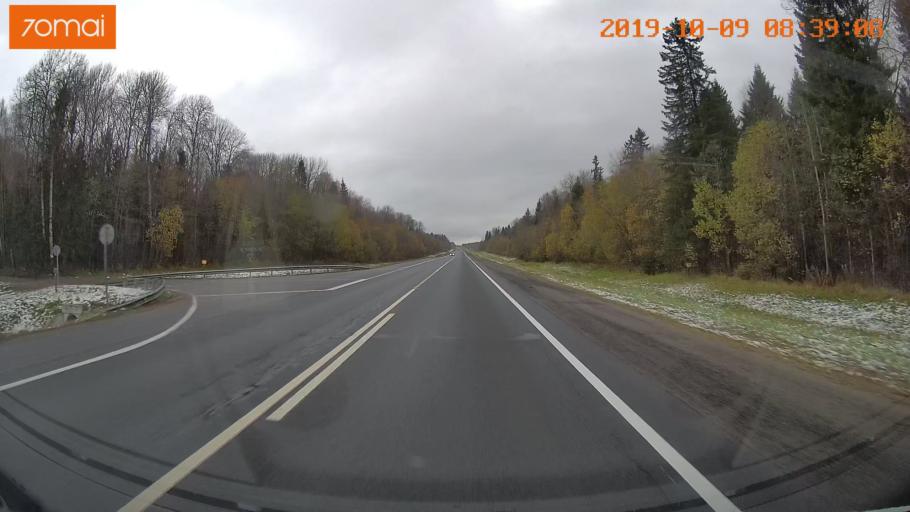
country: RU
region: Vologda
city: Gryazovets
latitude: 58.9668
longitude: 40.1570
